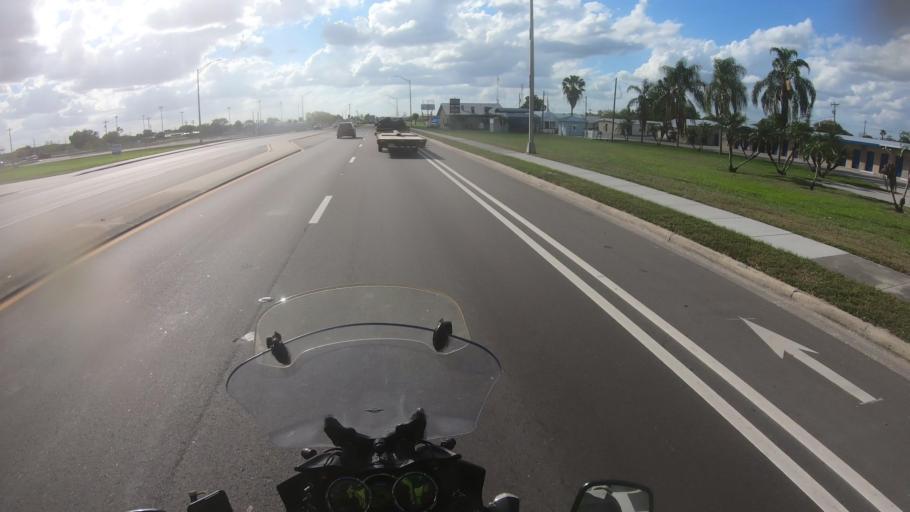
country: US
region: Florida
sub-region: Glades County
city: Moore Haven
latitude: 26.8446
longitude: -81.1005
